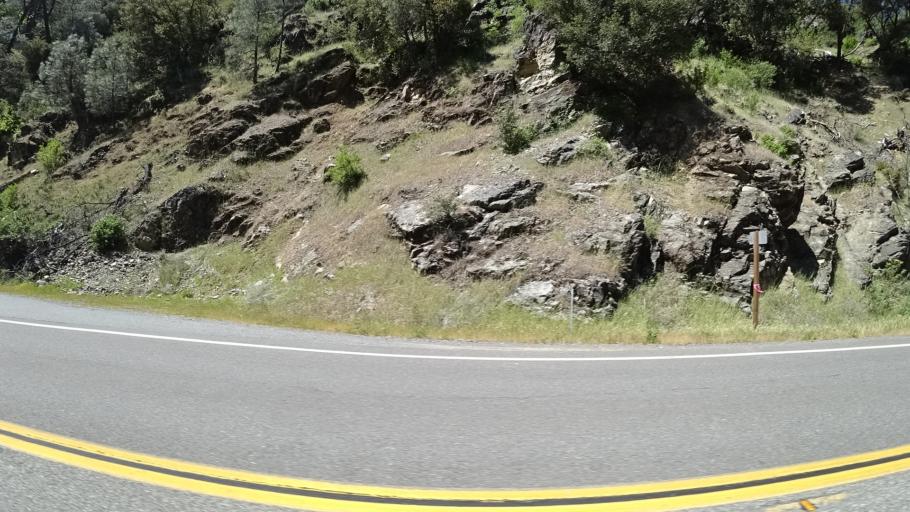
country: US
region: California
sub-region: Trinity County
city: Hayfork
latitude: 40.7513
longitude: -123.1661
